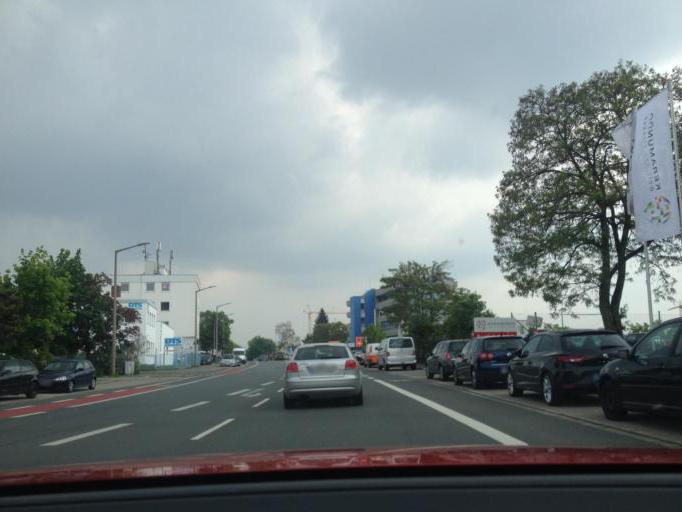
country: DE
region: Bavaria
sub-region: Regierungsbezirk Mittelfranken
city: Grossreuth bei Schweinau
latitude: 49.4451
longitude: 11.0098
